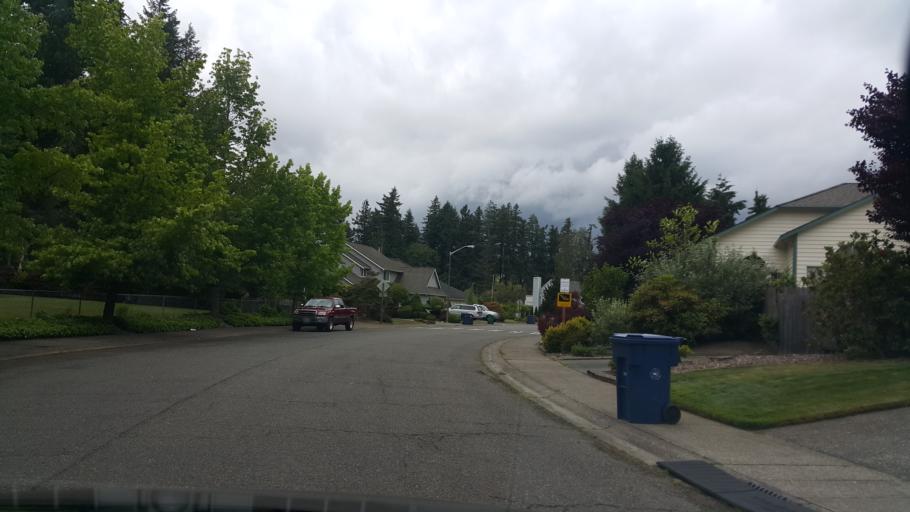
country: US
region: Washington
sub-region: King County
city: Fairwood
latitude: 47.4382
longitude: -122.1498
